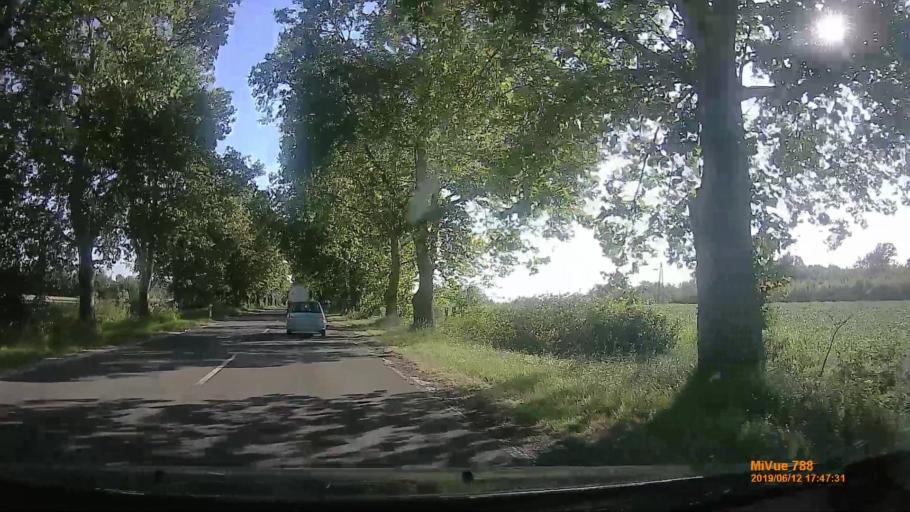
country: HU
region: Csongrad
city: Roszke
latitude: 46.2293
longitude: 20.0776
